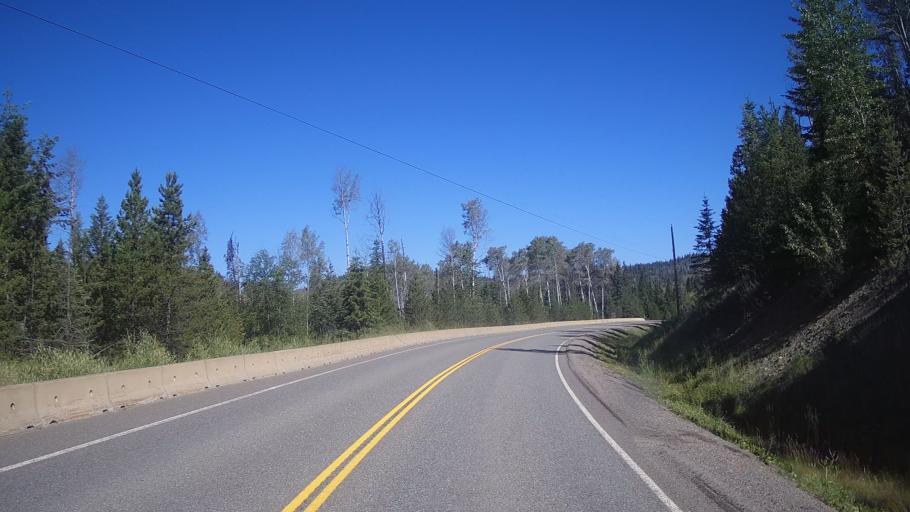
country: CA
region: British Columbia
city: Kamloops
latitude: 51.4786
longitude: -120.5619
